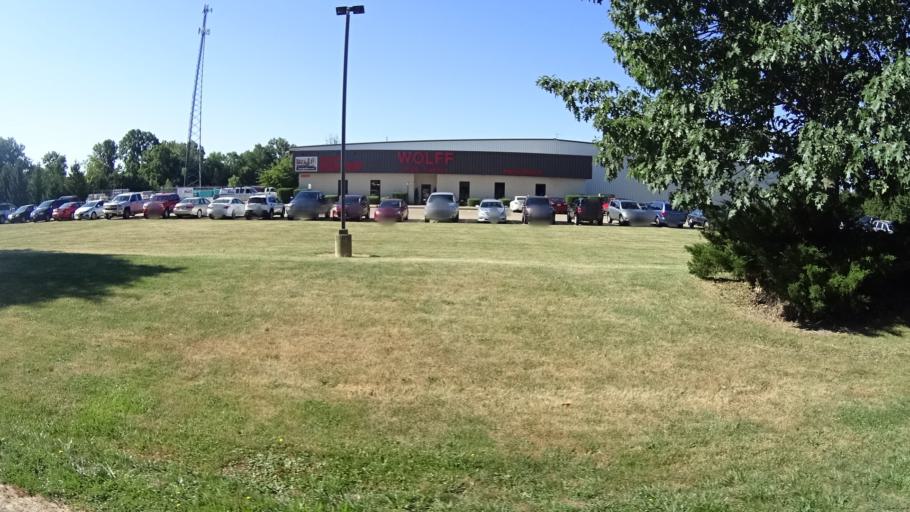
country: US
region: Ohio
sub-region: Erie County
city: Sandusky
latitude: 41.4096
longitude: -82.7344
